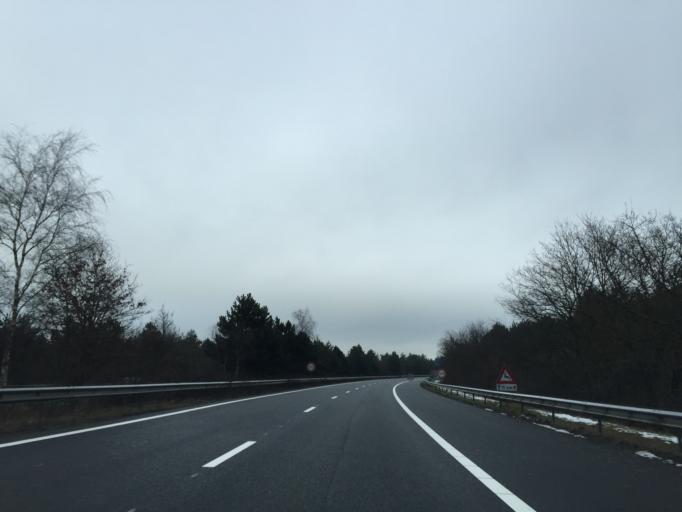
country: NL
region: Gelderland
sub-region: Gemeente Nunspeet
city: Nunspeet
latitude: 52.3817
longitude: 5.8275
